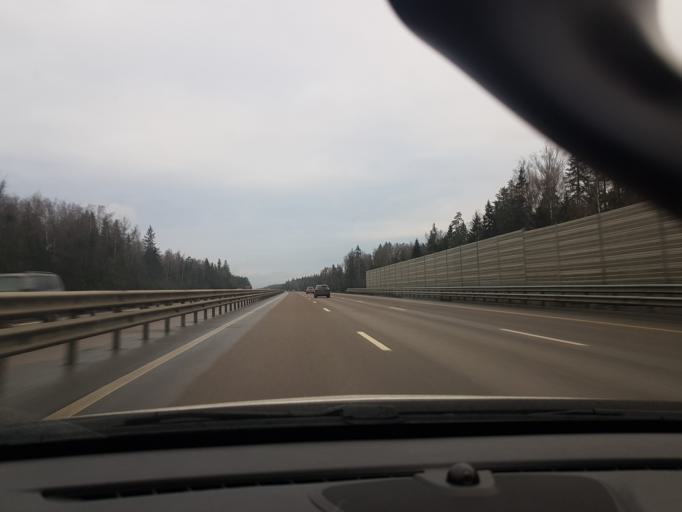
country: RU
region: Moskovskaya
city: Kostrovo
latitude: 55.8978
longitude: 36.6404
